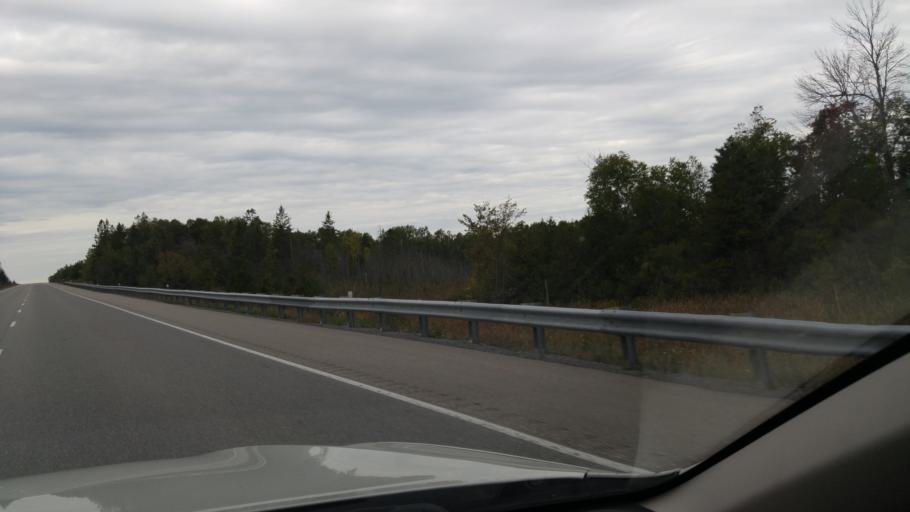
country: CA
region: Ontario
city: Carleton Place
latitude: 45.3259
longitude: -76.1242
